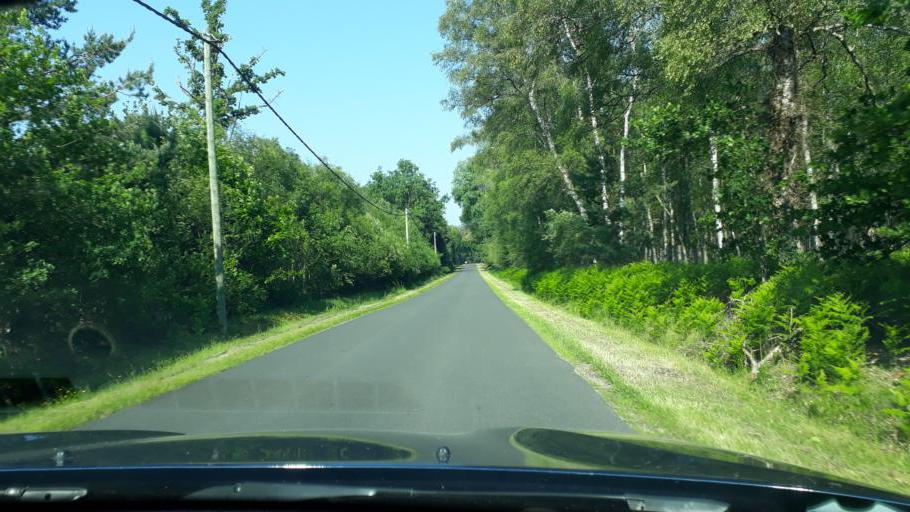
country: FR
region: Centre
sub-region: Departement du Loir-et-Cher
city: Dhuizon
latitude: 47.6224
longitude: 1.7291
